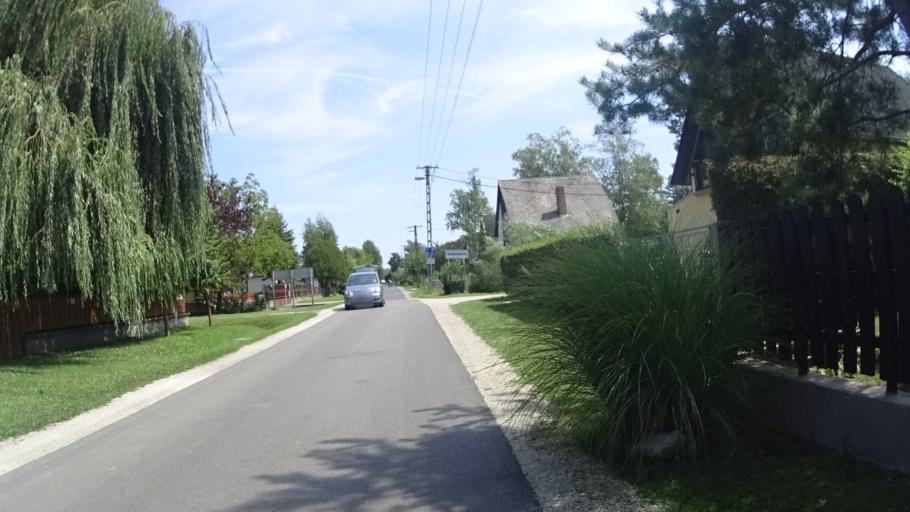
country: HU
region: Somogy
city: Balatonfenyves
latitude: 46.7059
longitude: 17.4376
